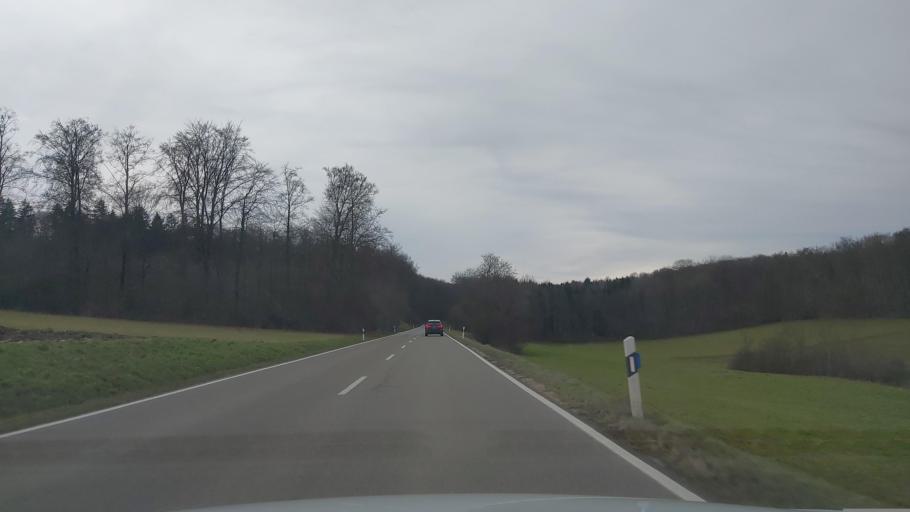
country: DE
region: Baden-Wuerttemberg
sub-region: Tuebingen Region
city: Allmendingen
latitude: 48.3040
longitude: 9.6851
